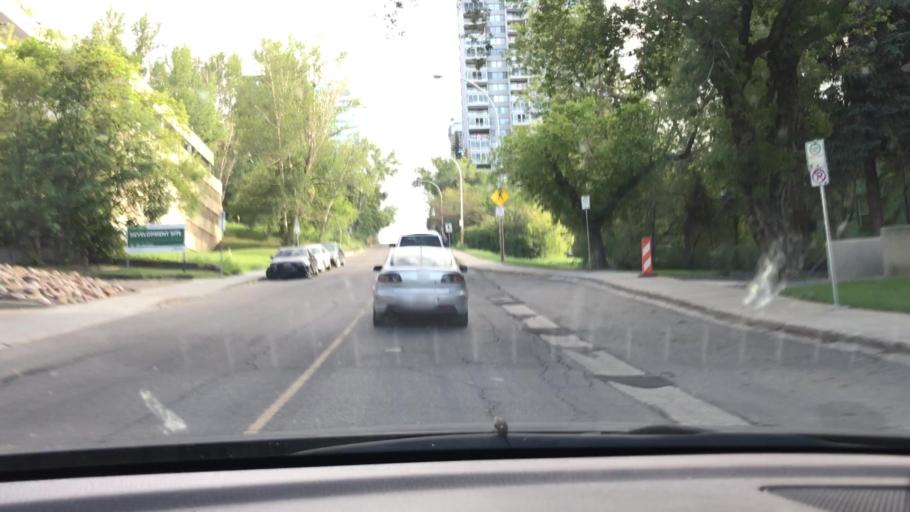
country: CA
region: Alberta
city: Edmonton
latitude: 53.5362
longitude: -113.4974
